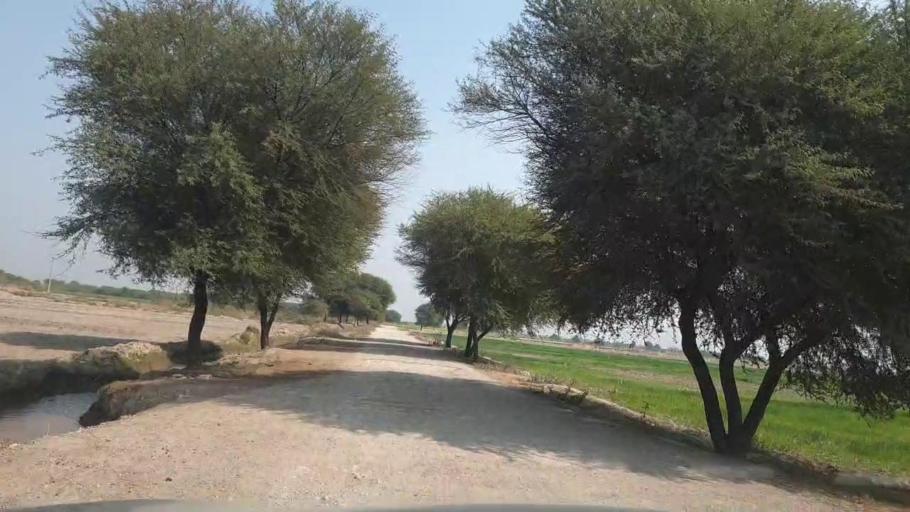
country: PK
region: Sindh
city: Tando Allahyar
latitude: 25.5642
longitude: 68.8189
